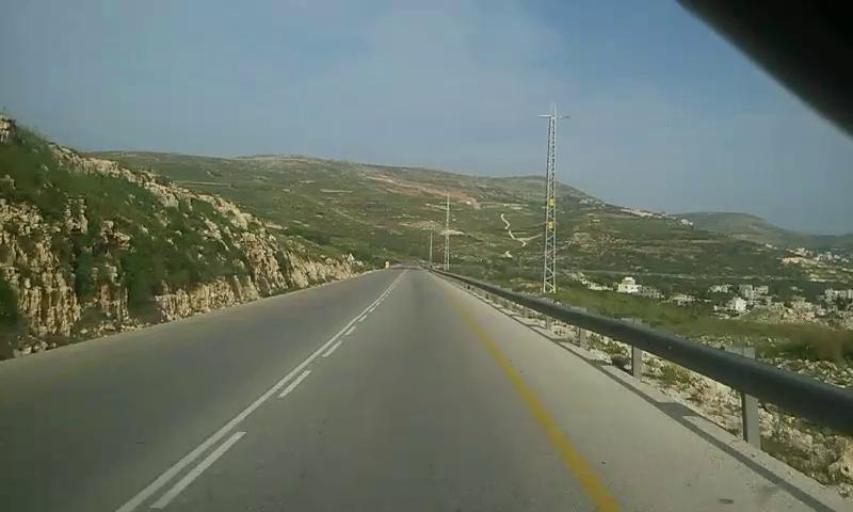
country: PS
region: West Bank
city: Madama
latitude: 32.1883
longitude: 35.2230
